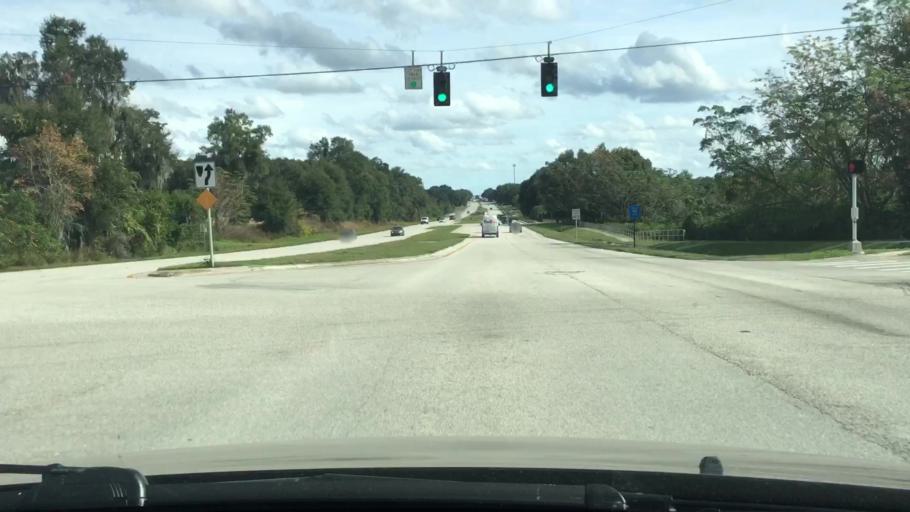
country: US
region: Florida
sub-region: Volusia County
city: North DeLand
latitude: 29.0545
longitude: -81.3168
